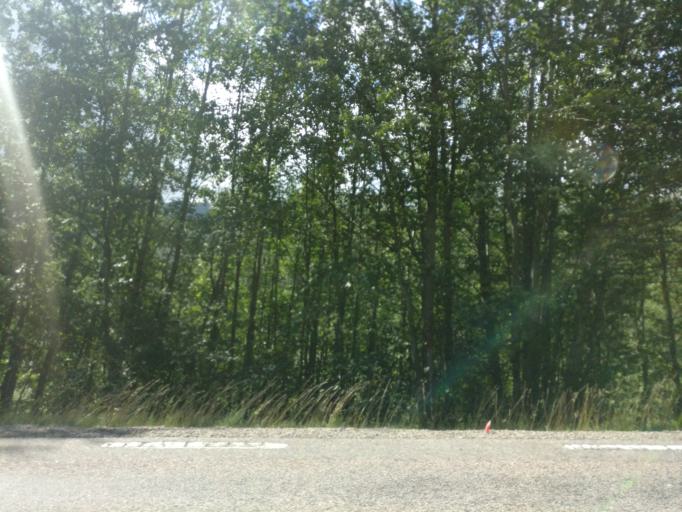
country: SE
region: Vaermland
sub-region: Hagfors Kommun
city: Ekshaerad
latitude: 60.3692
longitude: 13.3054
